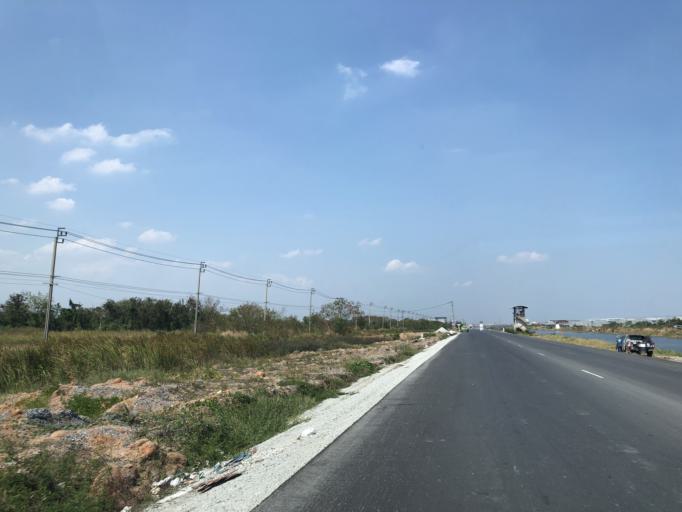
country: TH
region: Samut Prakan
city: Bang Bo District
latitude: 13.5464
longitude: 100.7516
